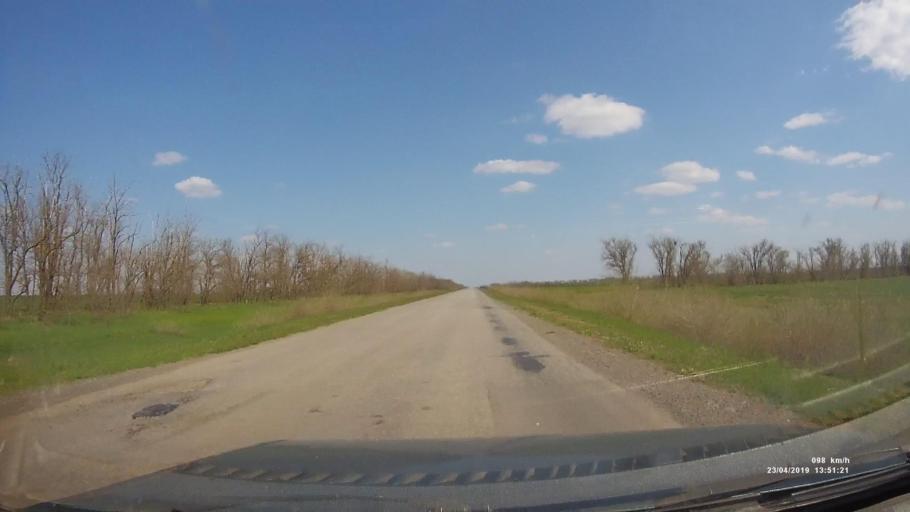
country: RU
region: Kalmykiya
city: Yashalta
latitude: 46.5995
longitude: 42.9325
